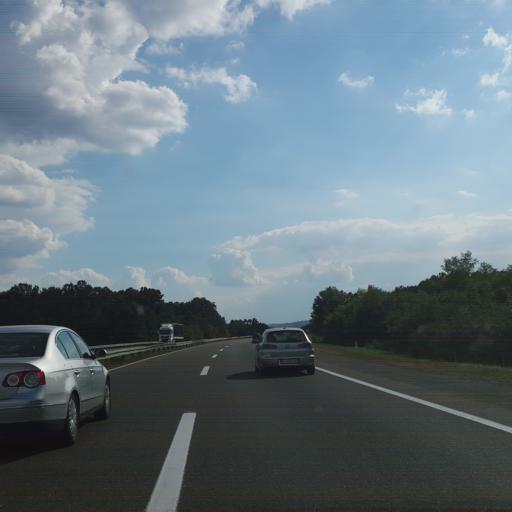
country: RS
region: Central Serbia
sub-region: Podunavski Okrug
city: Velika Plana
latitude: 44.3793
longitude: 21.0702
